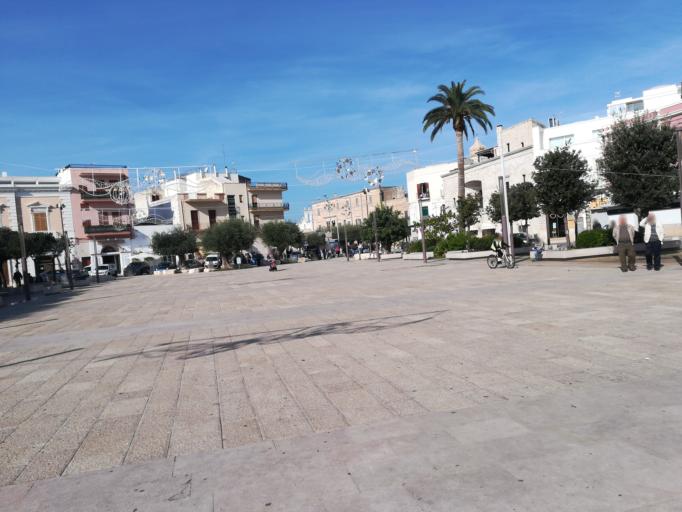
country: IT
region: Apulia
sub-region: Provincia di Bari
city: Polignano a Mare
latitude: 40.9944
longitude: 17.2203
